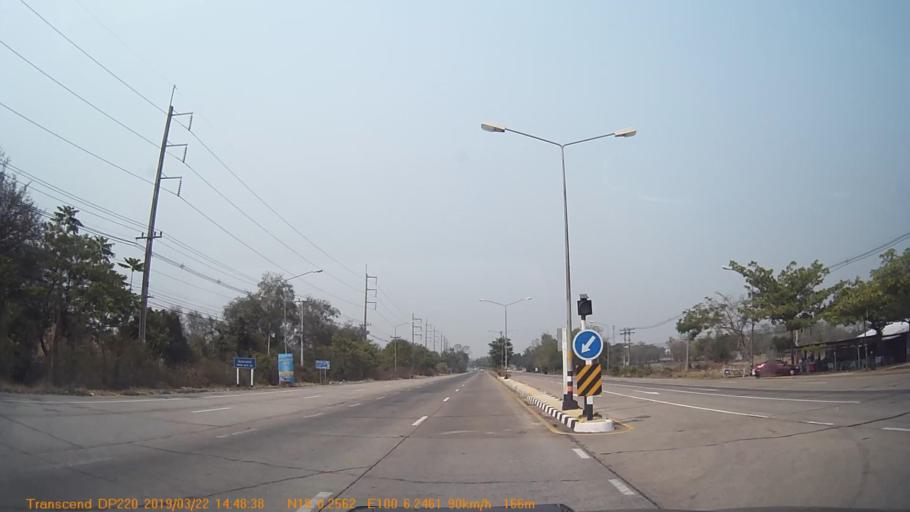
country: TH
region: Phrae
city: Sung Men
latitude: 18.0044
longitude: 100.1041
